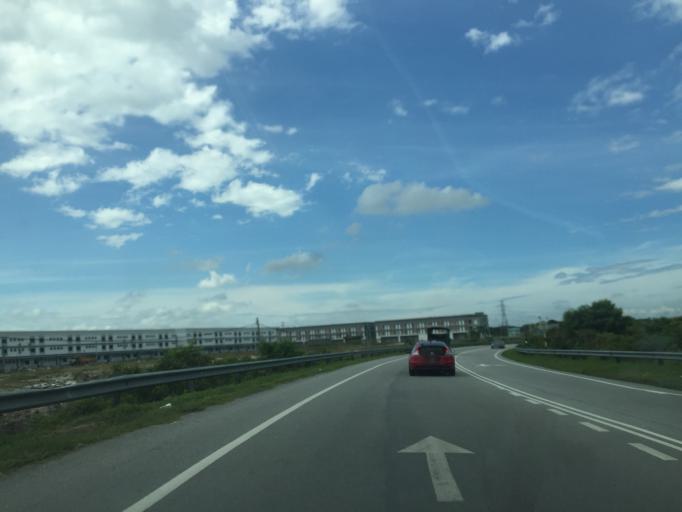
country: MY
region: Perak
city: Kampar
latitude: 4.3258
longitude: 101.1290
